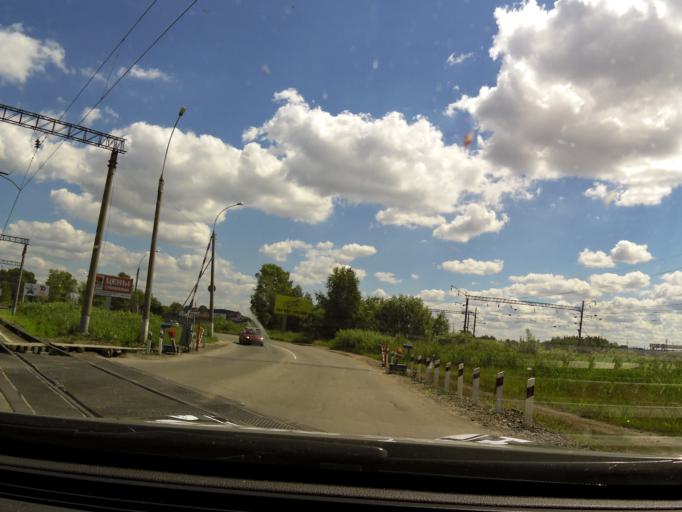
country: RU
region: Vologda
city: Vologda
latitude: 59.2330
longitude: 39.8368
